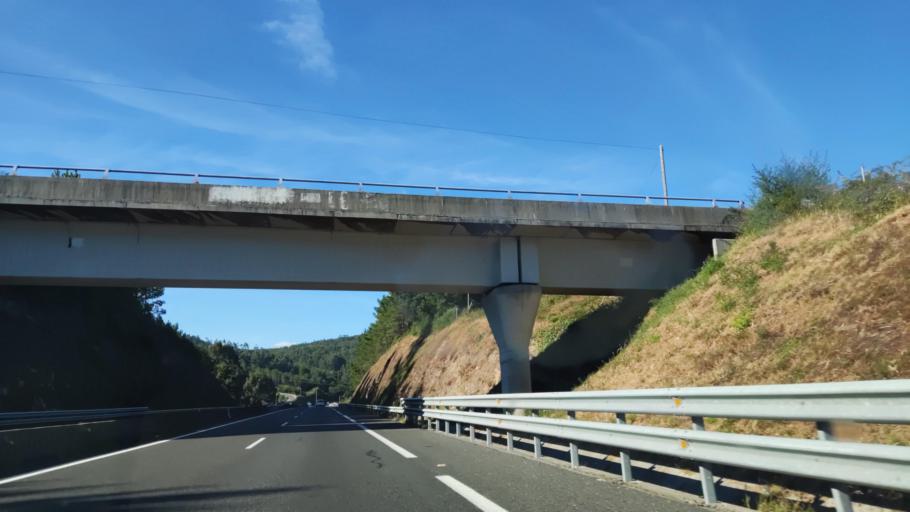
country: ES
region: Galicia
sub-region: Provincia da Coruna
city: Boiro
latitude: 42.6372
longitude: -8.9111
